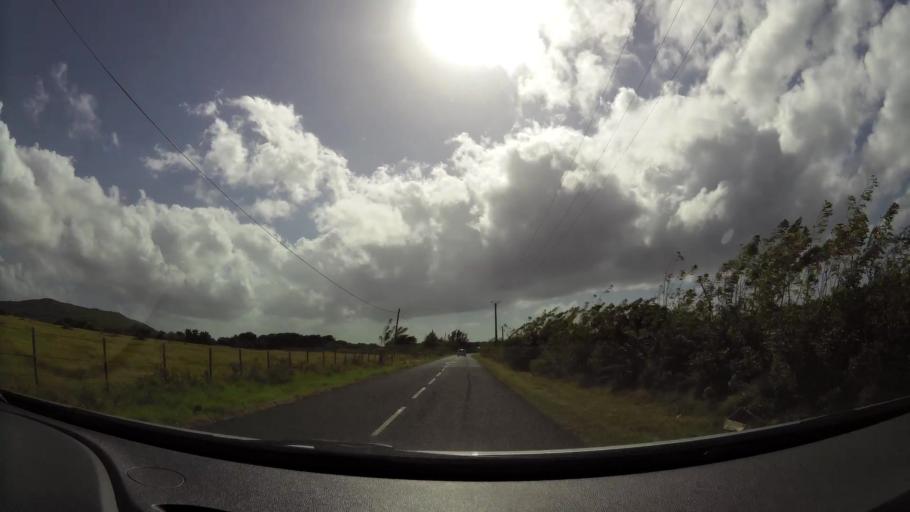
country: MQ
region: Martinique
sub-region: Martinique
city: Le Marin
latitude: 14.4079
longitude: -60.8768
